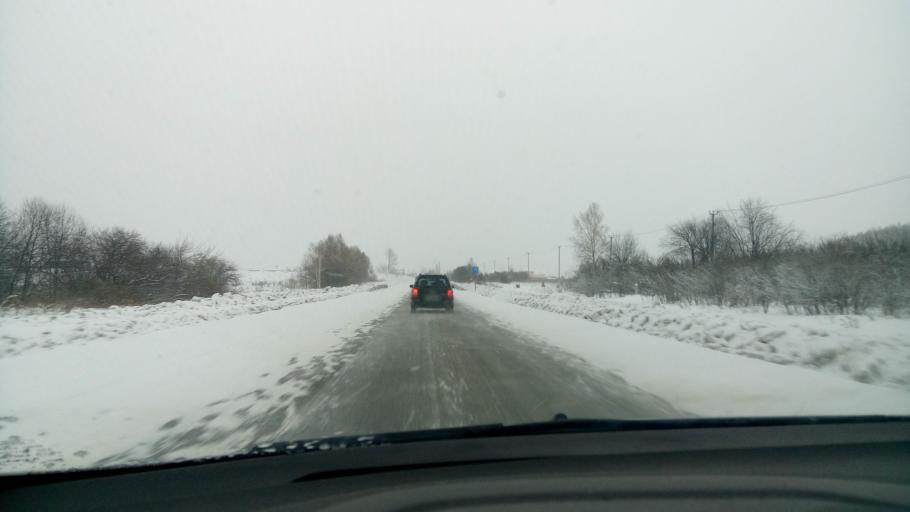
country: RU
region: Sverdlovsk
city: Verkhneye Dubrovo
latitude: 56.7358
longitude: 61.1029
